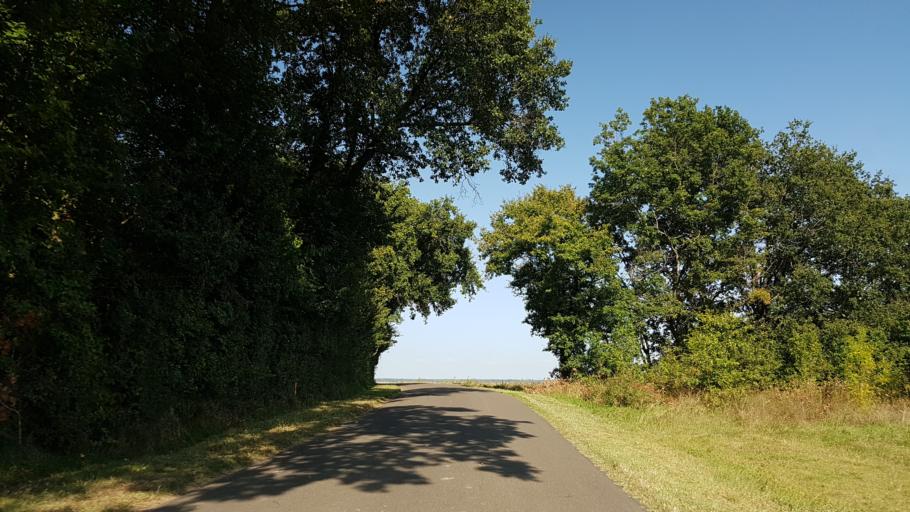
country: FR
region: Poitou-Charentes
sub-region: Departement de la Charente-Maritime
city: Breuillet
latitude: 45.7021
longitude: -1.0488
